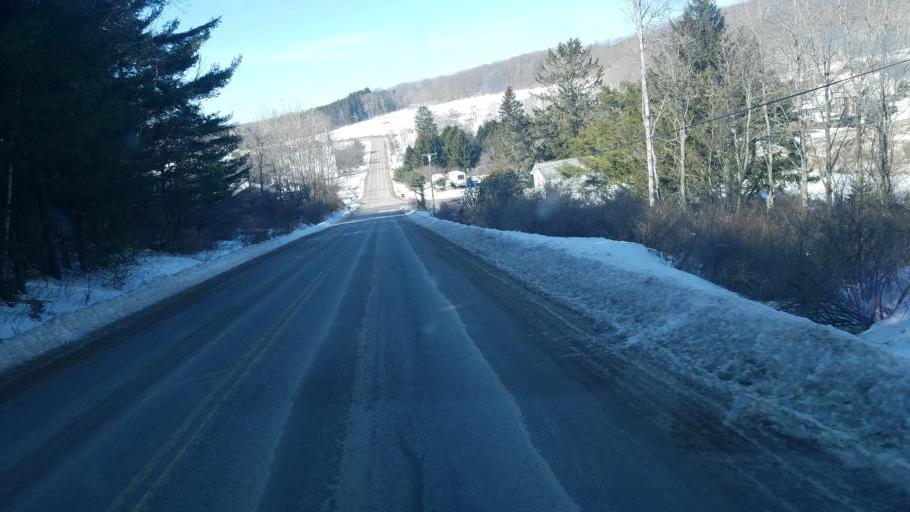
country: US
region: New York
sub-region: Allegany County
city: Andover
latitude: 42.0881
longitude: -77.7796
